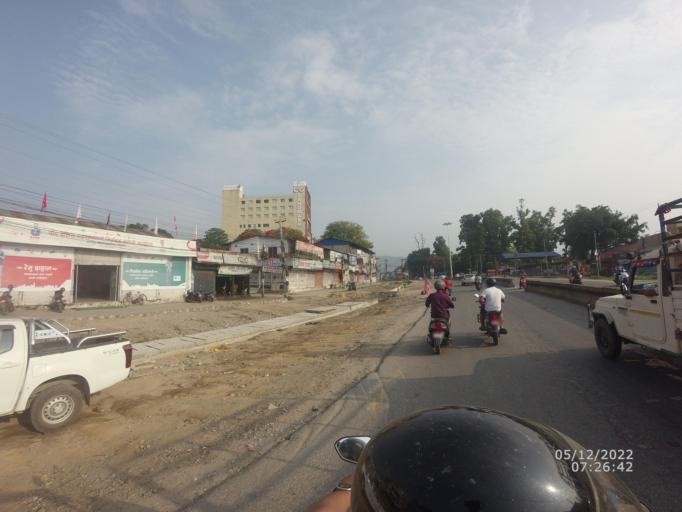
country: NP
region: Central Region
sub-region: Narayani Zone
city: Bharatpur
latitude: 27.6859
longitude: 84.4294
